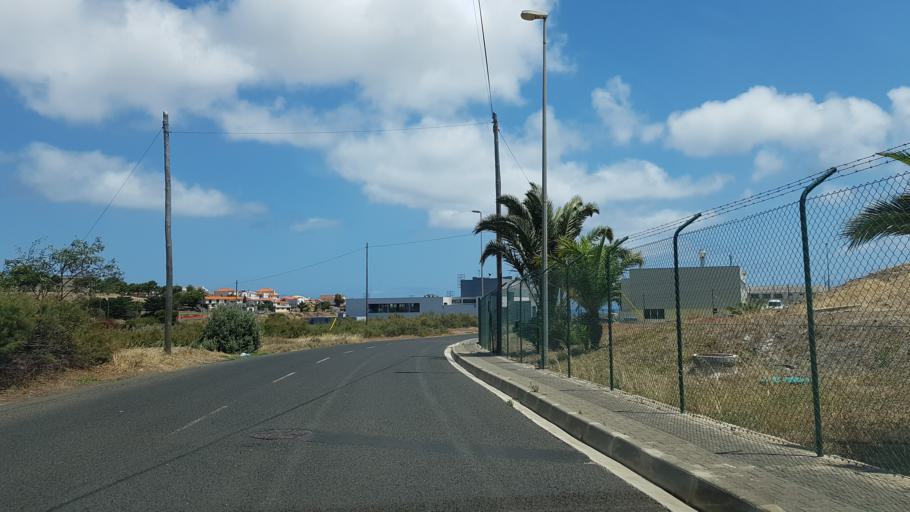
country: PT
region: Madeira
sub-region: Porto Santo
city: Camacha
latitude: 33.0731
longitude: -16.3445
